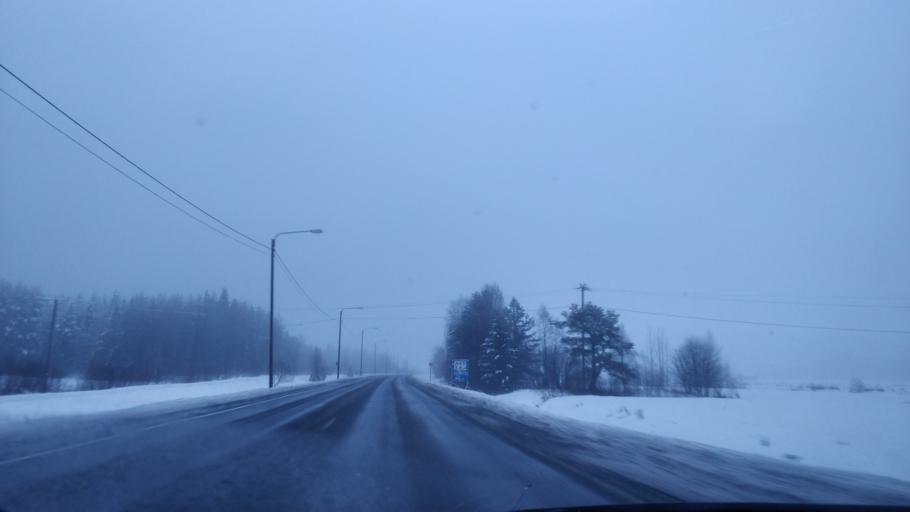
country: FI
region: Lapland
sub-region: Kemi-Tornio
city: Tervola
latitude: 66.1481
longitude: 24.9714
